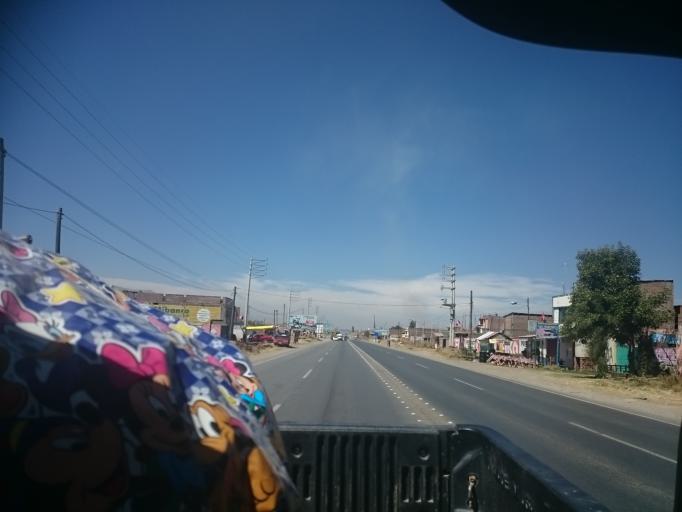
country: PE
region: Junin
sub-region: Provincia de Huancayo
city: San Agustin
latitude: -11.9764
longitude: -75.2657
